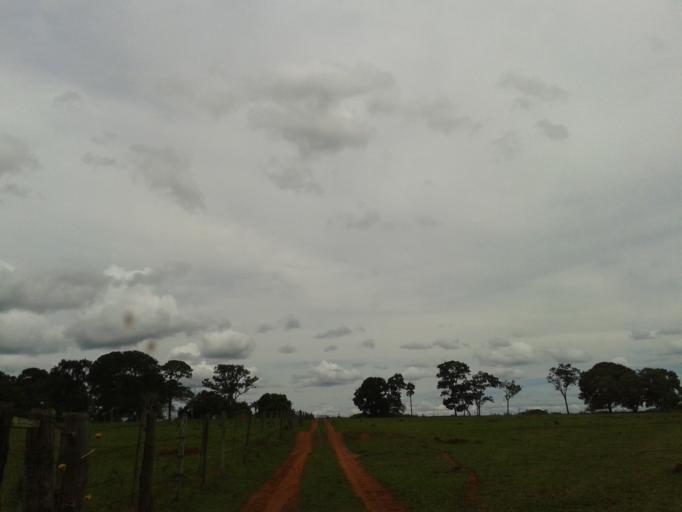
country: BR
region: Minas Gerais
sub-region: Santa Vitoria
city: Santa Vitoria
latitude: -18.7903
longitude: -49.8559
